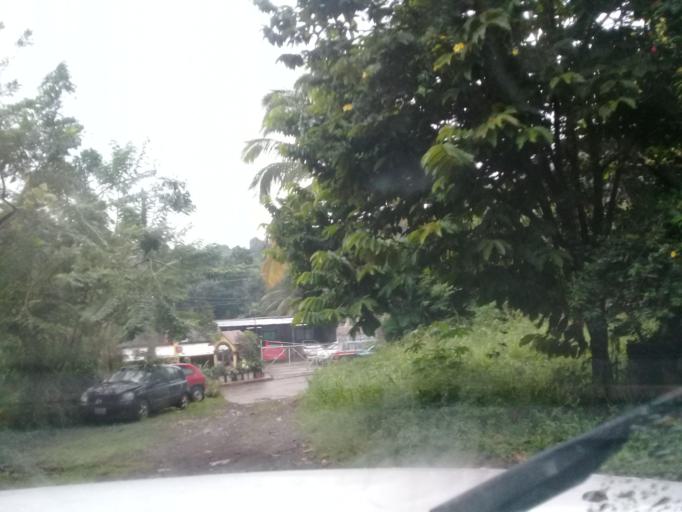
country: MX
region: Veracruz
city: San Andres Tuxtla
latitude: 18.4386
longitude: -95.1929
